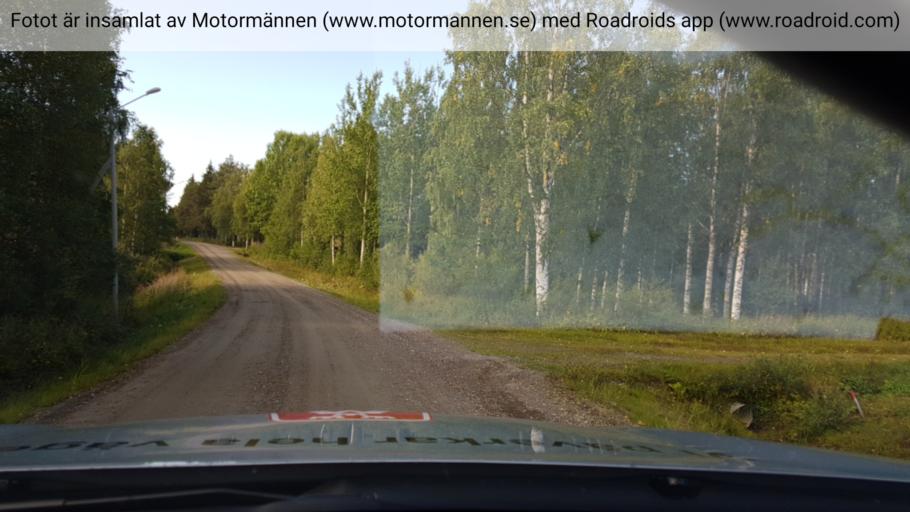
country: SE
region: Norrbotten
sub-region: Kalix Kommun
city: Kalix
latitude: 66.1116
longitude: 23.3002
